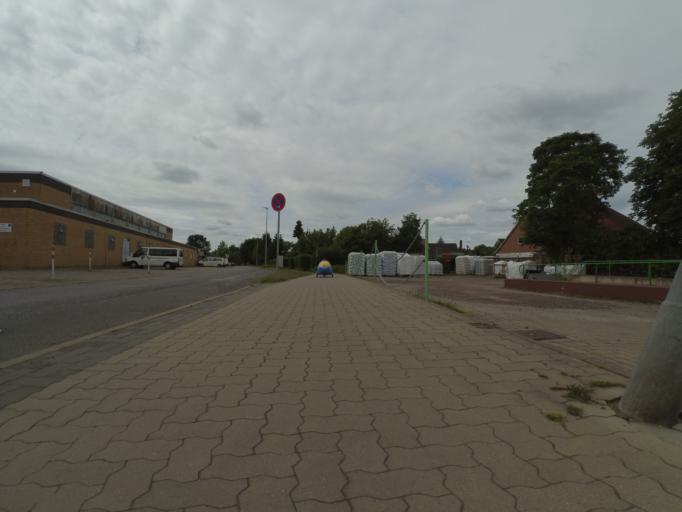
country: DE
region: Lower Saxony
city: Wunstorf
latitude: 52.4568
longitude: 9.3869
